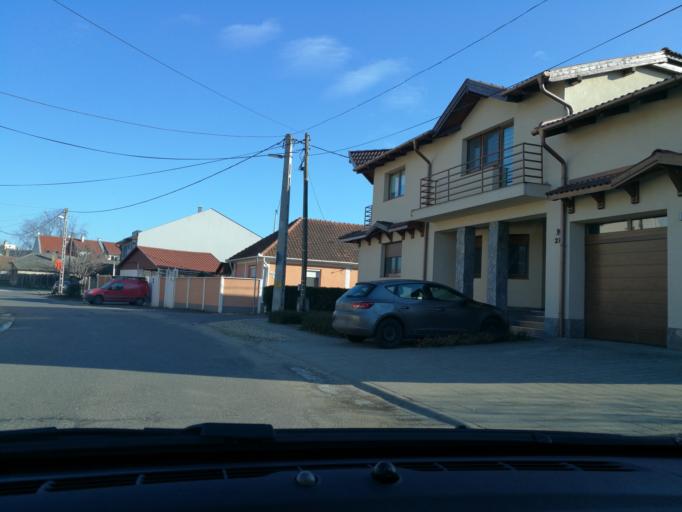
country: HU
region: Szabolcs-Szatmar-Bereg
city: Nyiregyhaza
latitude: 47.9443
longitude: 21.7226
